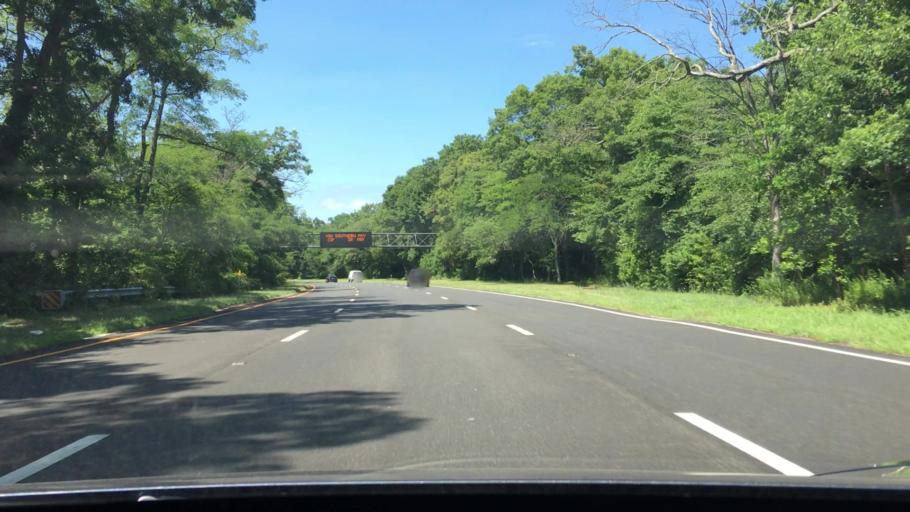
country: US
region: New York
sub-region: Nassau County
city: Wantagh
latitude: 40.6855
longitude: -73.5138
